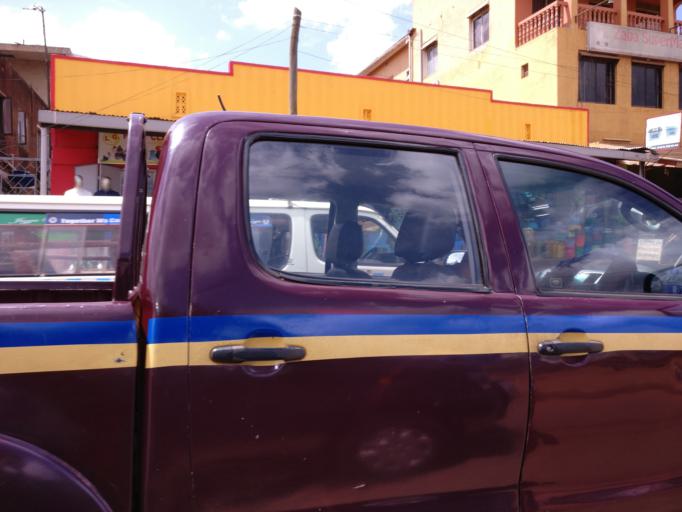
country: UG
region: Central Region
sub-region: Kampala District
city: Kampala
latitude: 0.2787
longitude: 32.5660
